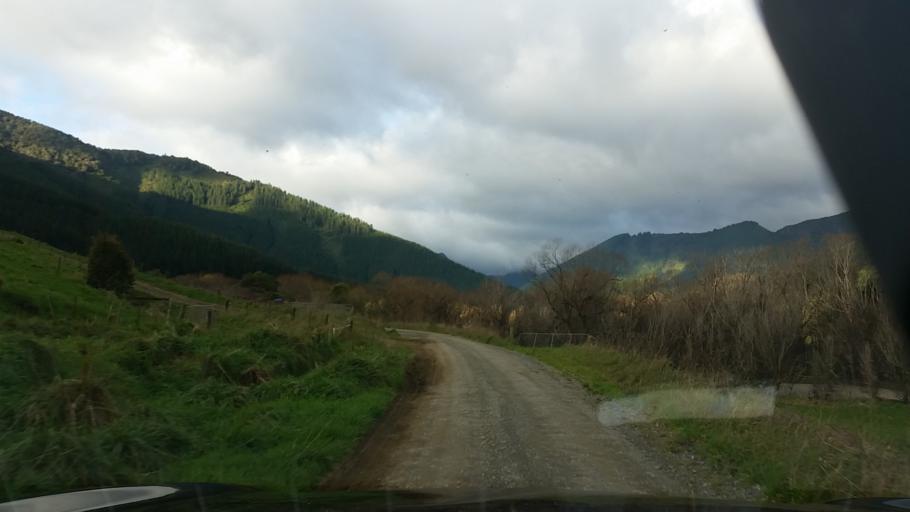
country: NZ
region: Nelson
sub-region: Nelson City
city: Nelson
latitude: -41.2103
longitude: 173.6301
